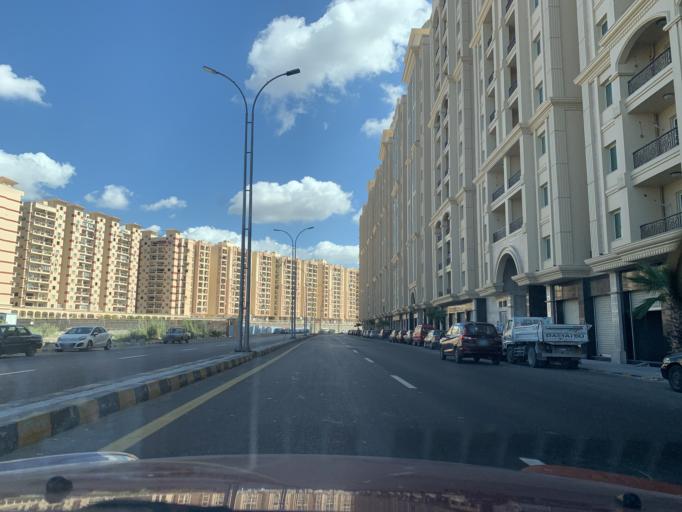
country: EG
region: Alexandria
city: Alexandria
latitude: 31.2145
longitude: 29.9556
